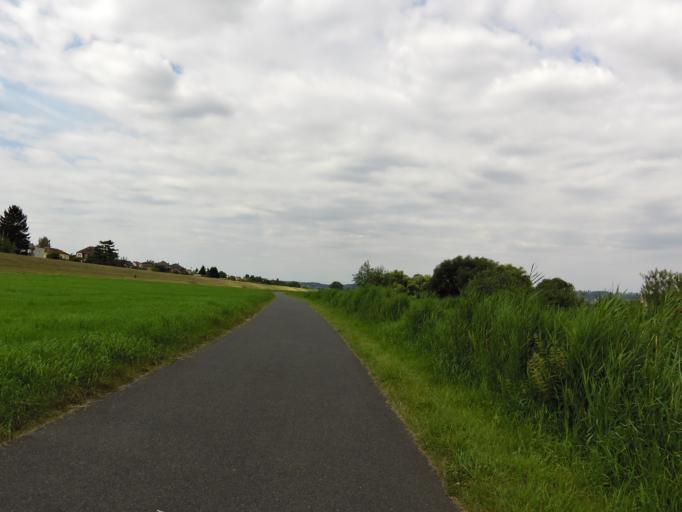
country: DE
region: Saxony
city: Radebeul
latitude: 51.0745
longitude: 13.6702
